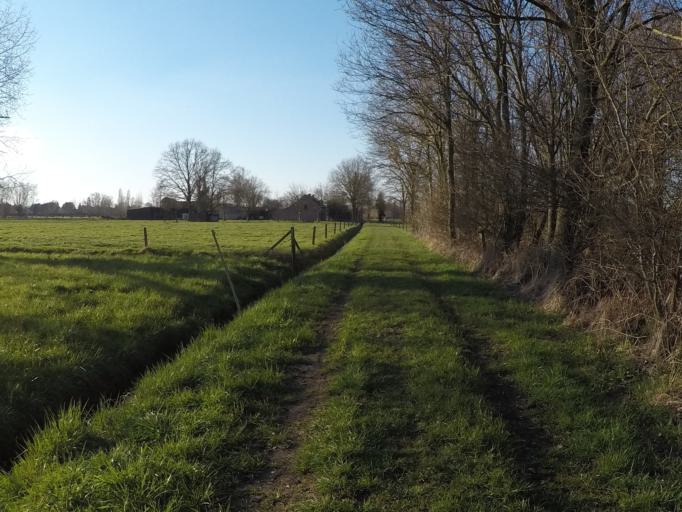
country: BE
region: Flanders
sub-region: Provincie Antwerpen
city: Lier
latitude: 51.1144
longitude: 4.5957
